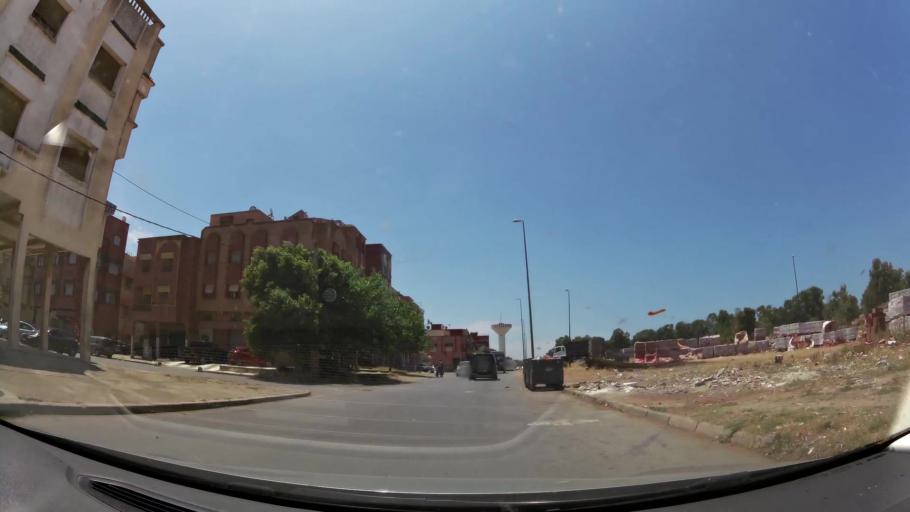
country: MA
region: Gharb-Chrarda-Beni Hssen
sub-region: Kenitra Province
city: Kenitra
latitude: 34.2583
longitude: -6.6267
